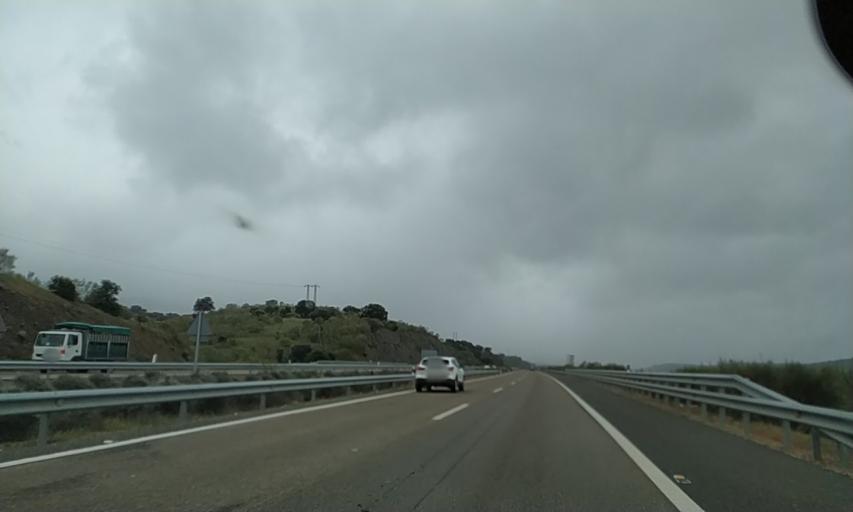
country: ES
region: Extremadura
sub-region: Provincia de Caceres
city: Riolobos
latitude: 39.8749
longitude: -6.2891
